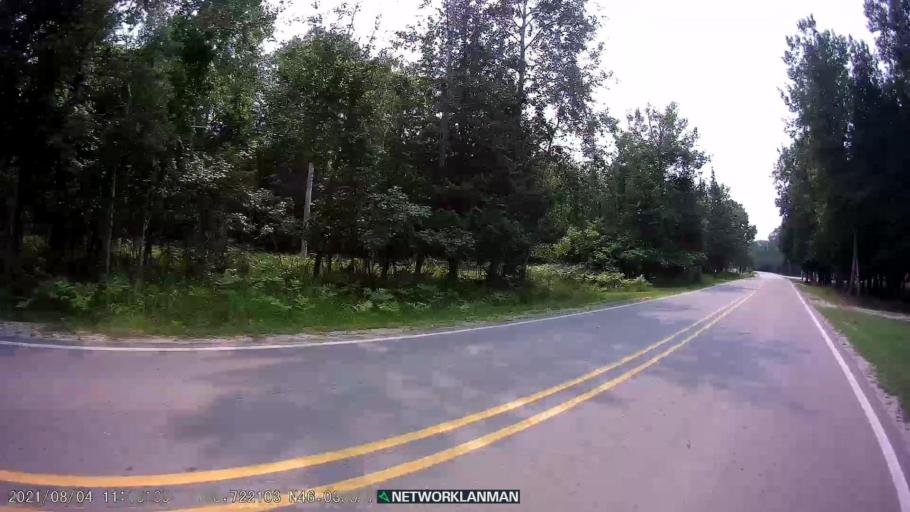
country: CA
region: Ontario
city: Thessalon
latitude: 46.0353
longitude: -83.7222
